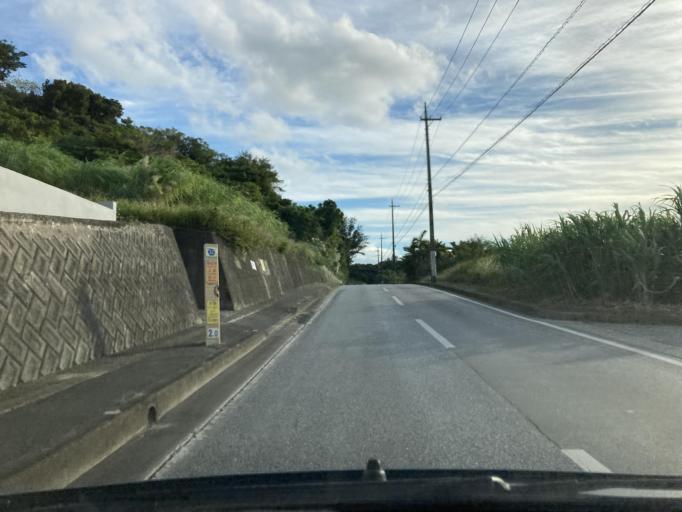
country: JP
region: Okinawa
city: Tomigusuku
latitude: 26.1484
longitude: 127.7447
